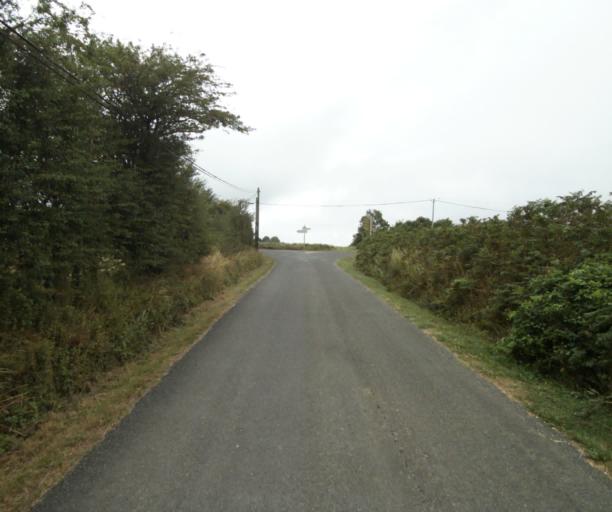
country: FR
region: Midi-Pyrenees
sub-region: Departement du Tarn
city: Soreze
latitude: 43.4064
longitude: 2.0578
